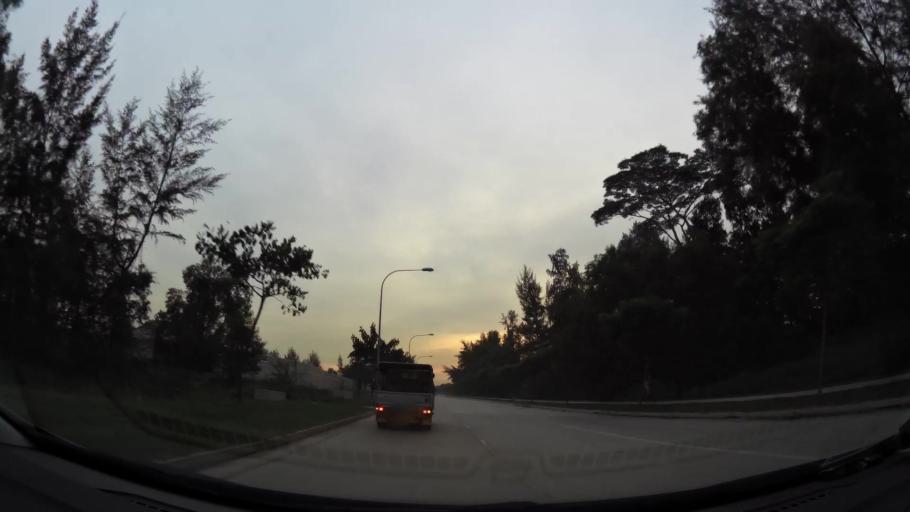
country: SG
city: Singapore
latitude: 1.2904
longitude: 103.8811
